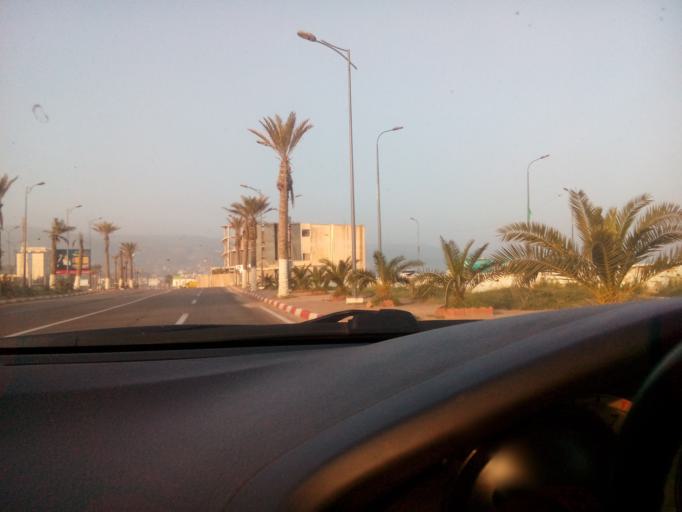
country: DZ
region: Oran
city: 'Ain el Turk
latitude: 35.7072
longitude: -0.8813
